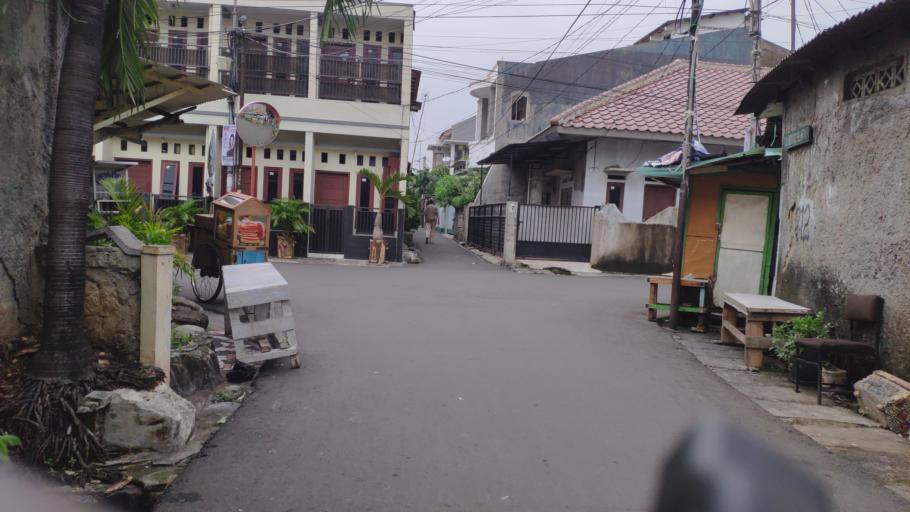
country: ID
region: Jakarta Raya
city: Jakarta
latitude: -6.2153
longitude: 106.8404
